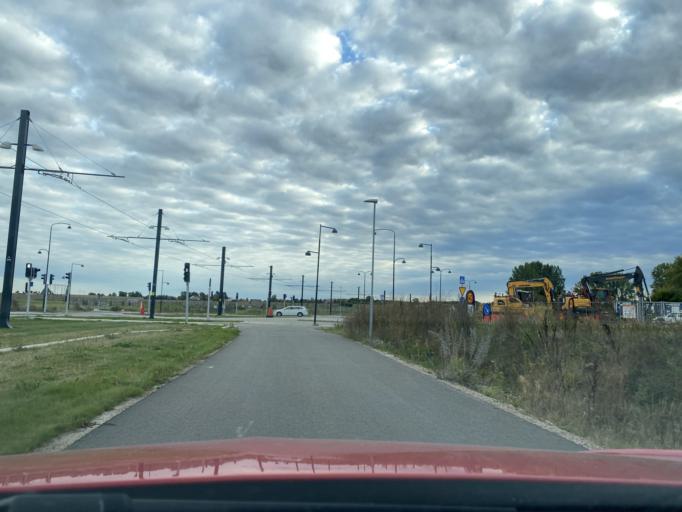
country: SE
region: Skane
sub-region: Lunds Kommun
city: Lund
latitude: 55.7296
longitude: 13.2419
